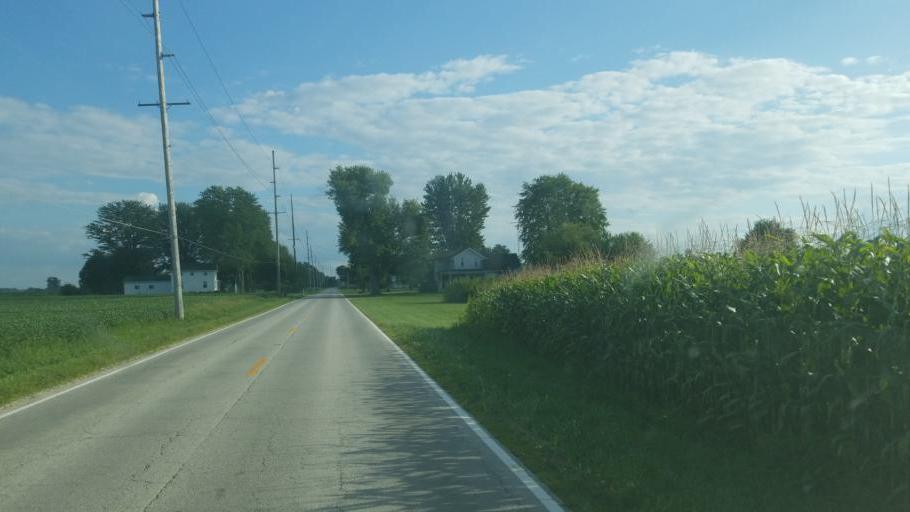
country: US
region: Ohio
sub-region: Sandusky County
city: Ballville
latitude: 41.2884
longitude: -83.1302
